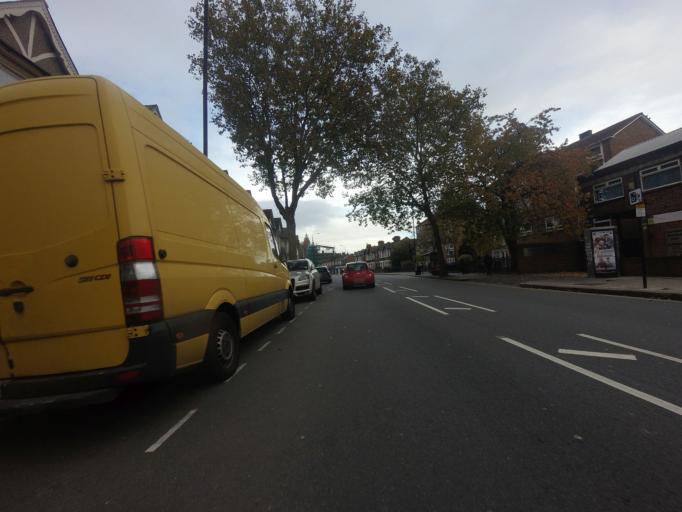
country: GB
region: England
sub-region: Greater London
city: East Ham
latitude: 51.5303
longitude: 0.0558
